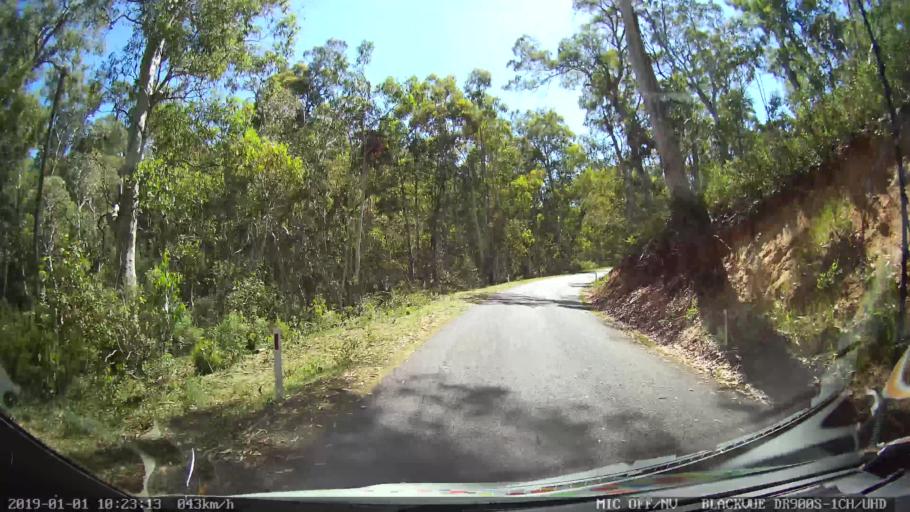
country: AU
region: New South Wales
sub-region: Snowy River
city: Jindabyne
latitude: -36.0752
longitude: 148.2097
